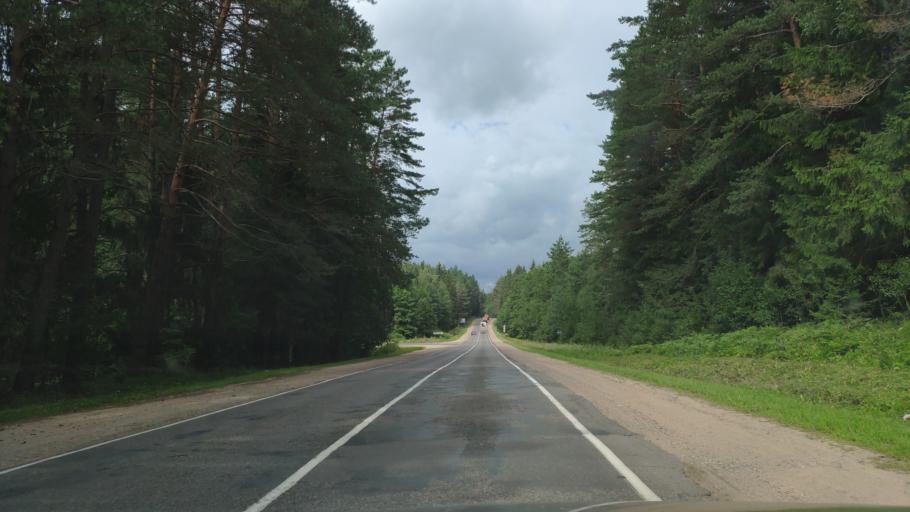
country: BY
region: Minsk
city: Zaslawye
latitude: 53.9730
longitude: 27.2484
